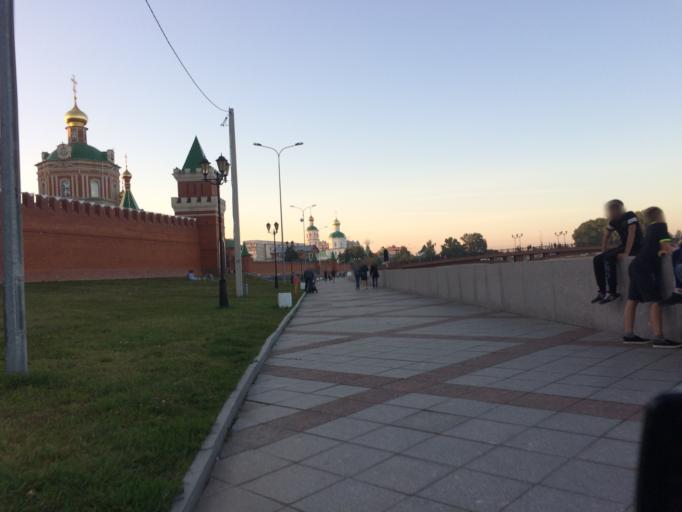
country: RU
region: Mariy-El
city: Yoshkar-Ola
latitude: 56.6359
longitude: 47.9039
